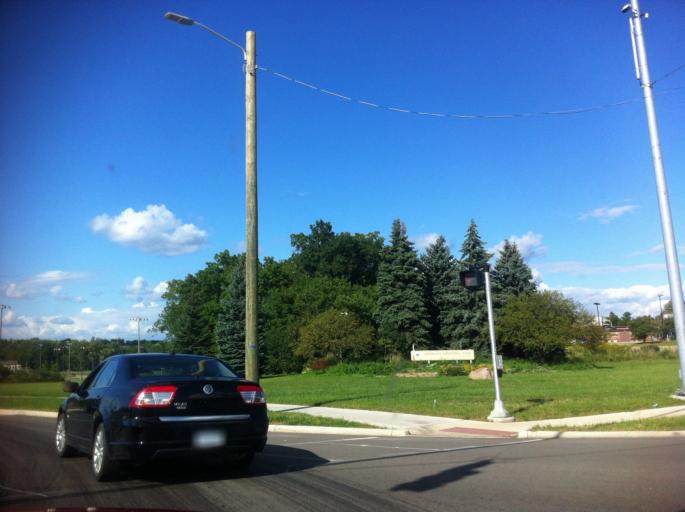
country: US
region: Michigan
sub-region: Washtenaw County
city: Ann Arbor
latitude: 42.2806
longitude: -83.7803
